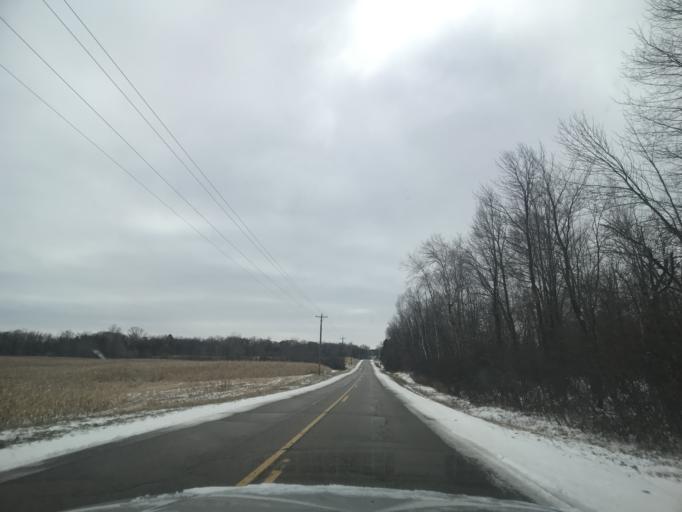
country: US
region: Wisconsin
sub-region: Brown County
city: Suamico
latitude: 44.7160
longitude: -88.0709
